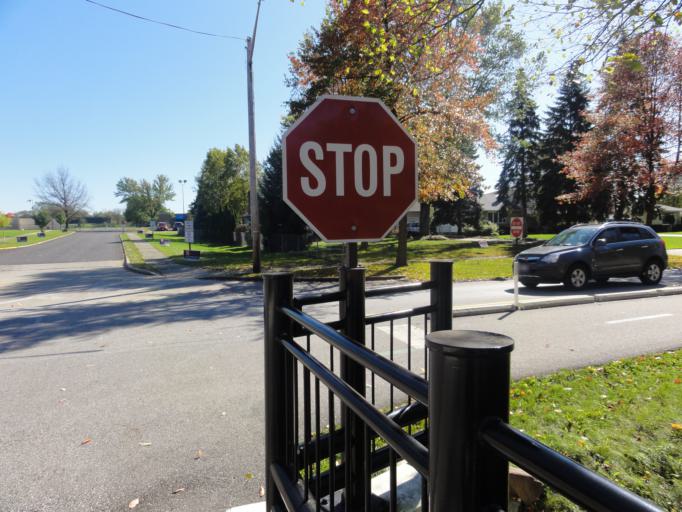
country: US
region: Ohio
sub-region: Cuyahoga County
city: Middleburg Heights
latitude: 41.3689
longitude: -81.8100
